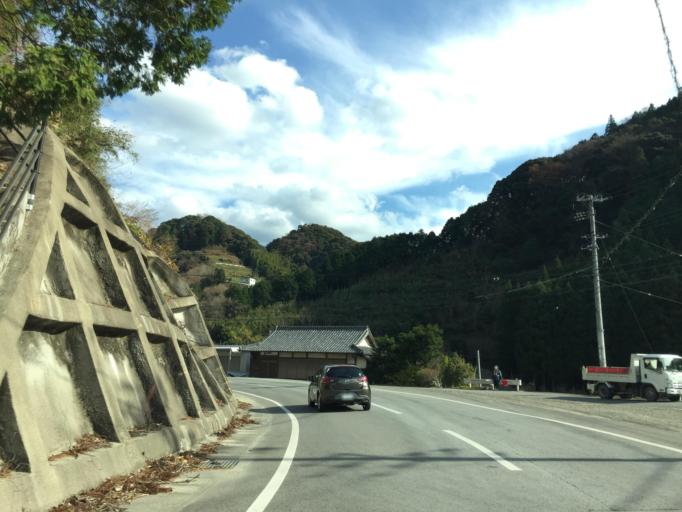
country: JP
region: Wakayama
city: Iwade
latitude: 34.1357
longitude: 135.3973
